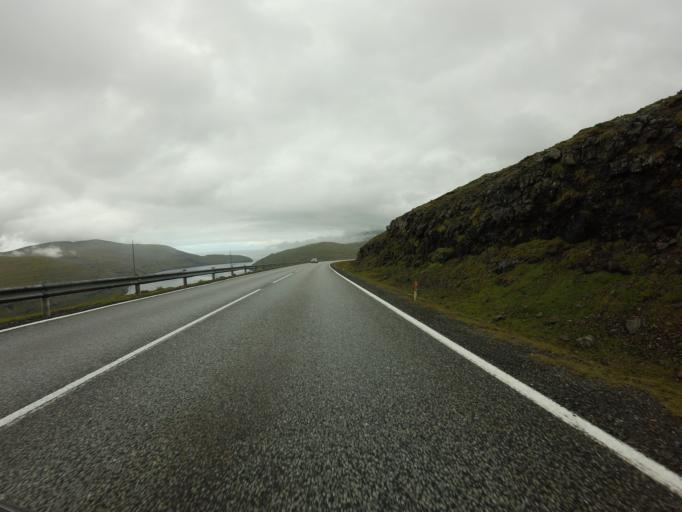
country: FO
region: Streymoy
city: Vestmanna
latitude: 62.1293
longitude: -7.1553
